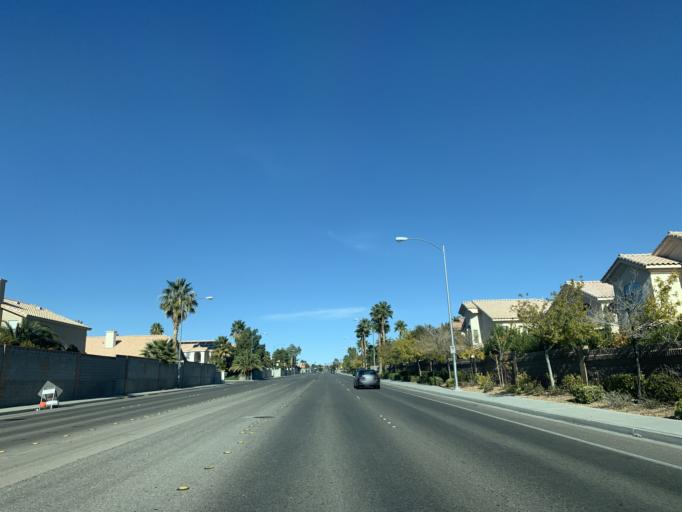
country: US
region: Nevada
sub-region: Clark County
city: Summerlin South
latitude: 36.1192
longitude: -115.2879
